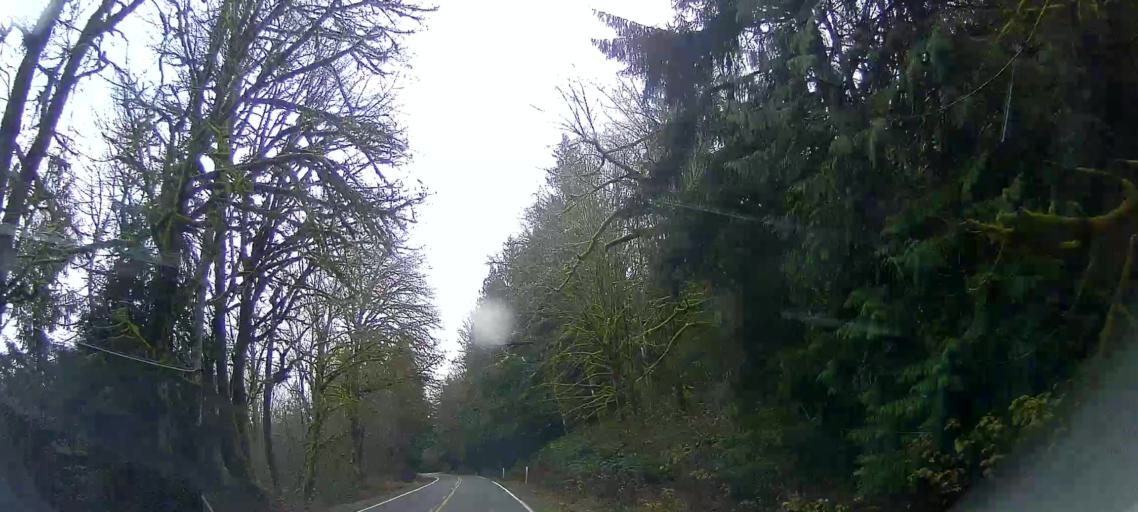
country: US
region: Washington
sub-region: Skagit County
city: Sedro-Woolley
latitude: 48.5119
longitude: -121.9306
